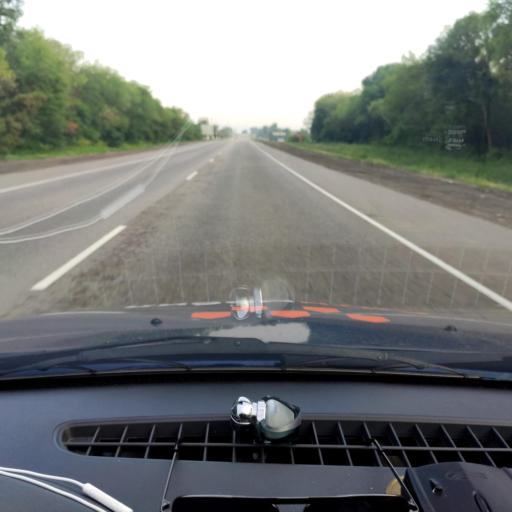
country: RU
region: Lipetsk
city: Yelets
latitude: 52.5496
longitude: 38.7118
